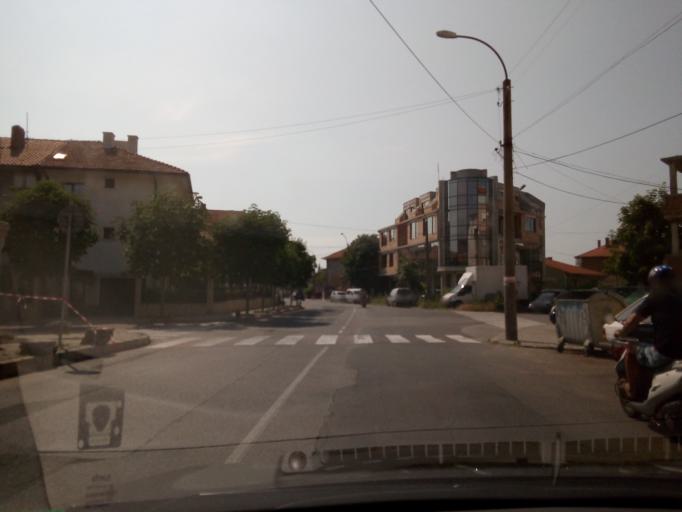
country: BG
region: Burgas
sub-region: Obshtina Pomorie
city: Pomorie
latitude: 42.5703
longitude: 27.6137
